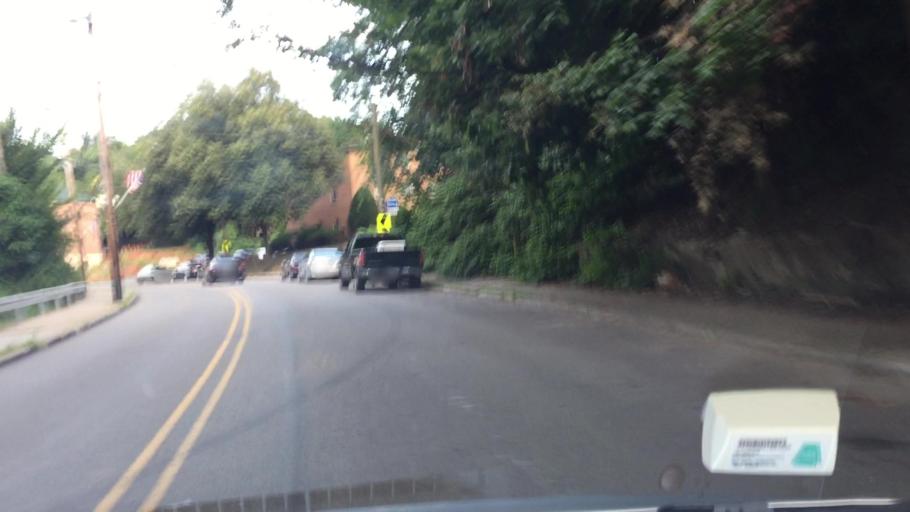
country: US
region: Pennsylvania
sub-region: Allegheny County
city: Homestead
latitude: 40.4245
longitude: -79.9377
